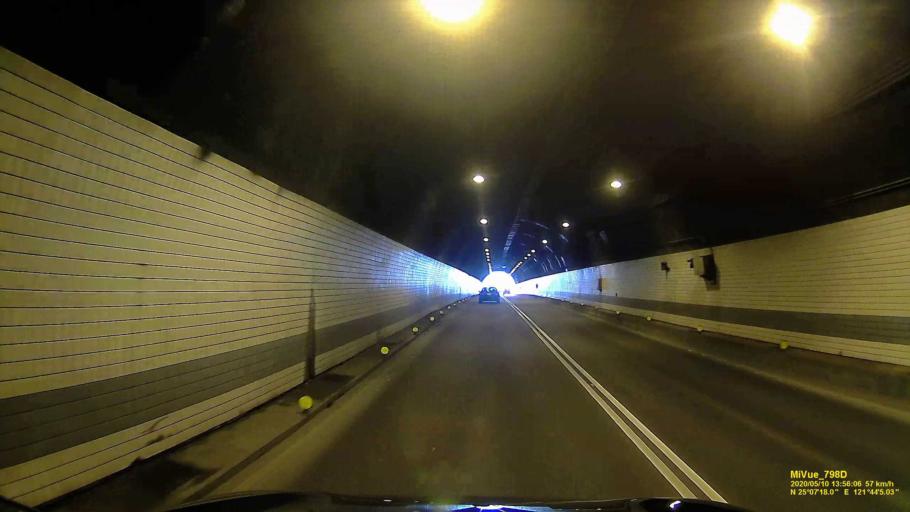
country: TW
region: Taiwan
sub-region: Keelung
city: Keelung
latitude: 25.1205
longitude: 121.7337
